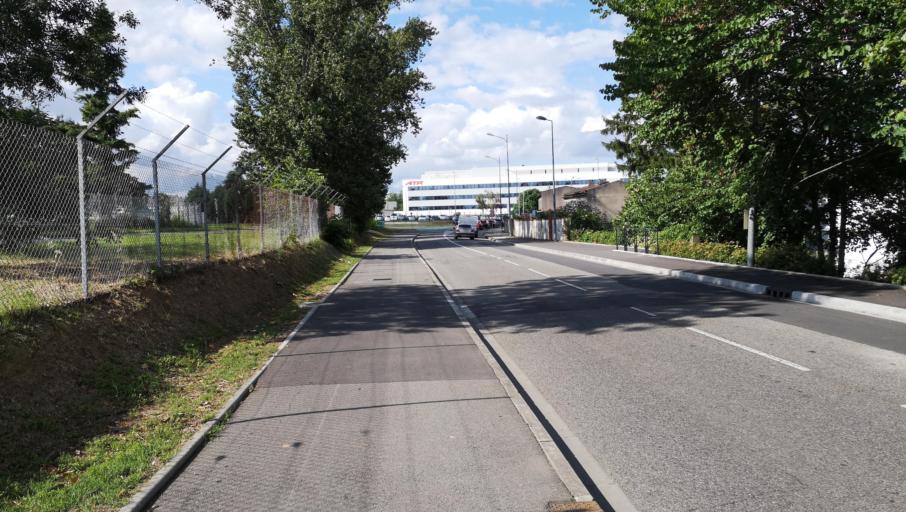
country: FR
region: Midi-Pyrenees
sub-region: Departement de la Haute-Garonne
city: Blagnac
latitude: 43.6192
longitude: 1.3892
